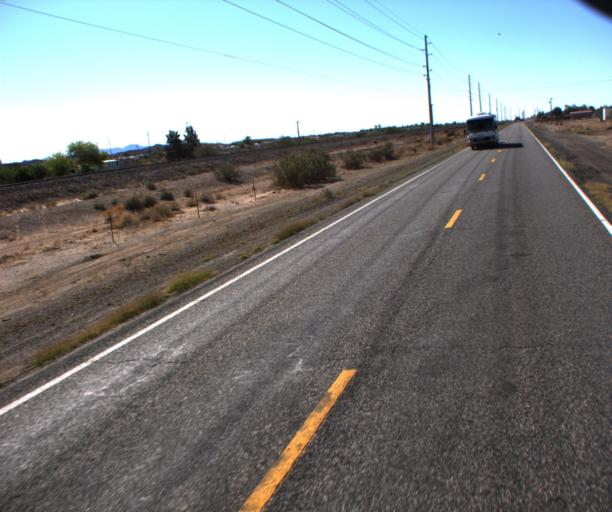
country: US
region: Arizona
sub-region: La Paz County
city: Cienega Springs
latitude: 33.9434
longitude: -114.0140
